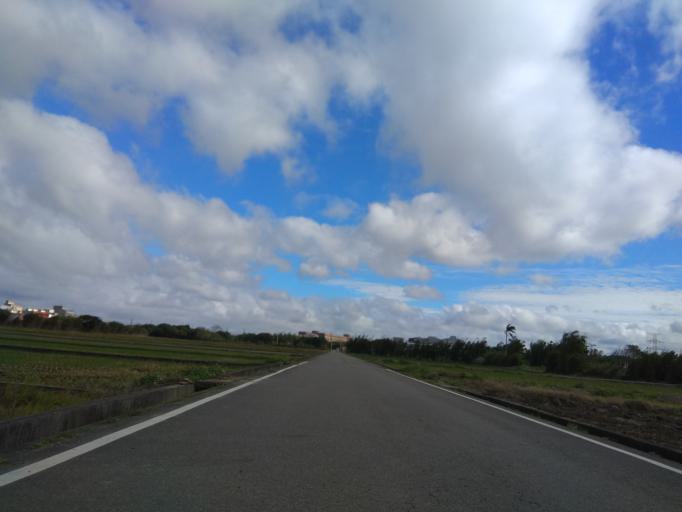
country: TW
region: Taiwan
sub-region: Hsinchu
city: Zhubei
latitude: 24.9706
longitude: 121.0823
